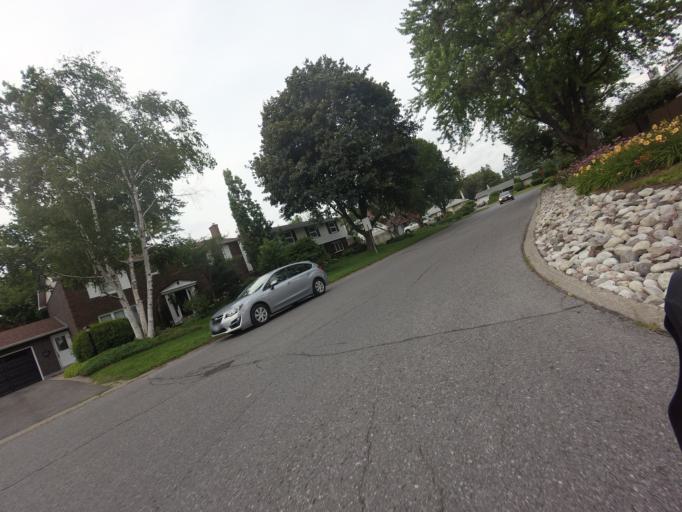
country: CA
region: Ontario
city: Ottawa
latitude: 45.3643
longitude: -75.7257
